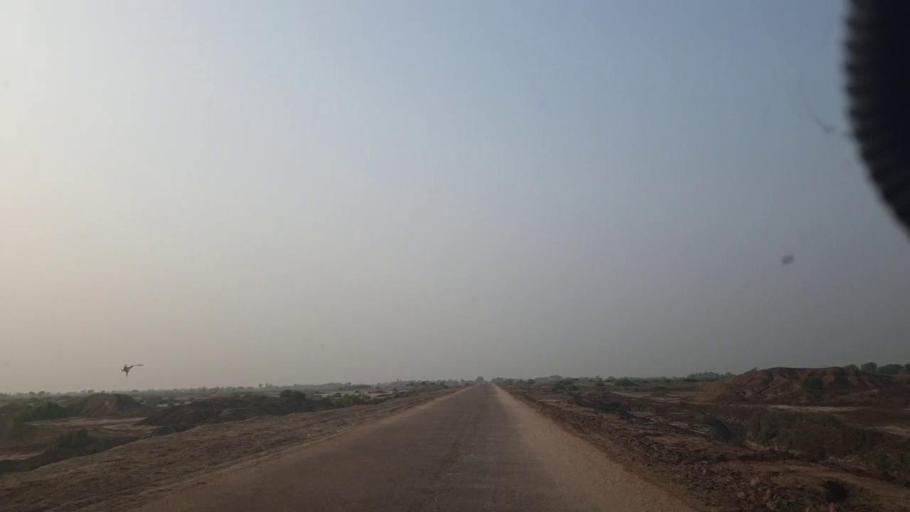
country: PK
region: Sindh
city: Bulri
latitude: 24.8551
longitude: 68.4026
